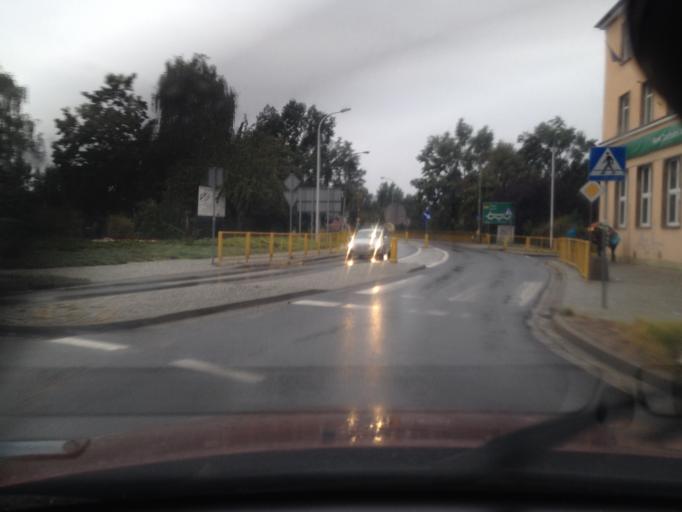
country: PL
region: Lubusz
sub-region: Powiat zaganski
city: Zagan
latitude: 51.6169
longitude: 15.3176
